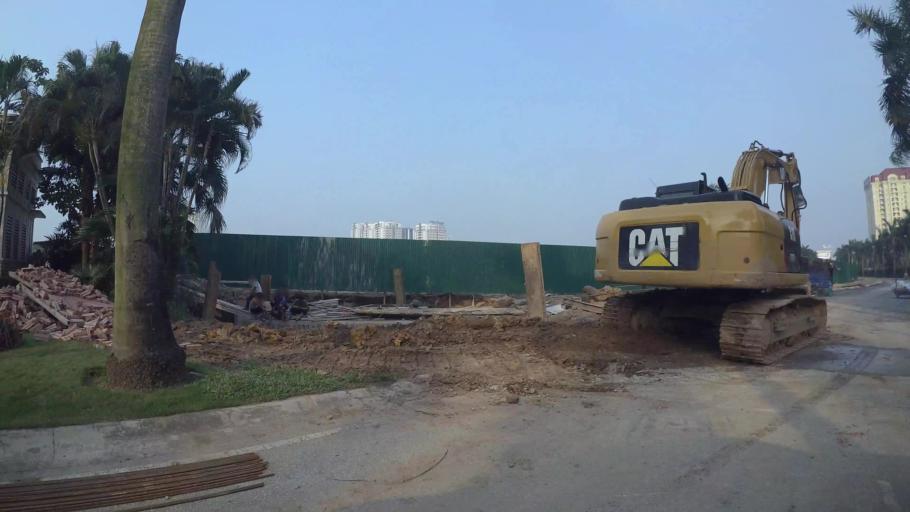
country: VN
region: Ha Noi
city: Tay Ho
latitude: 21.0766
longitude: 105.8074
